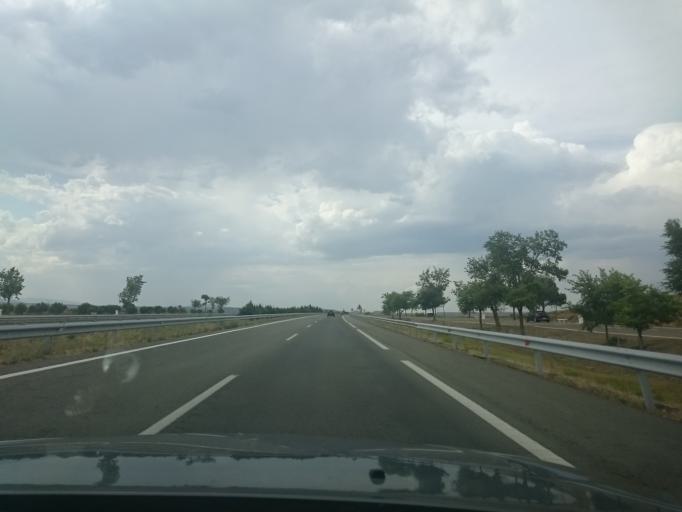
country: ES
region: Navarre
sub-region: Provincia de Navarra
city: Corella
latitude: 42.1640
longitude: -1.8253
